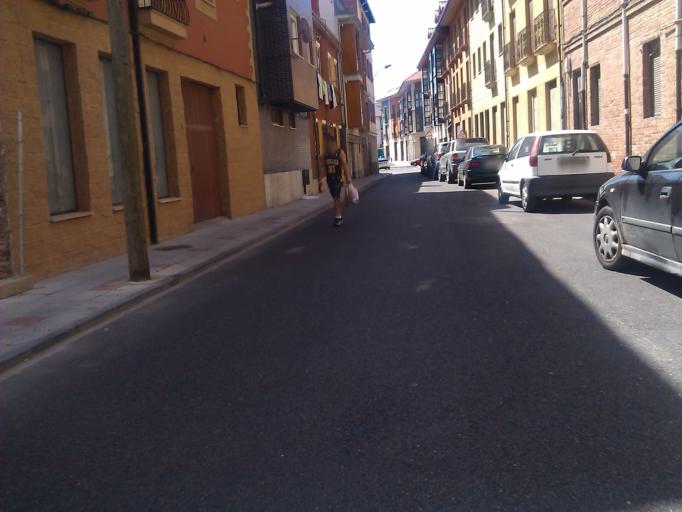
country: ES
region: Castille and Leon
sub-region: Provincia de Leon
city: Leon
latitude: 42.6023
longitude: -5.5671
